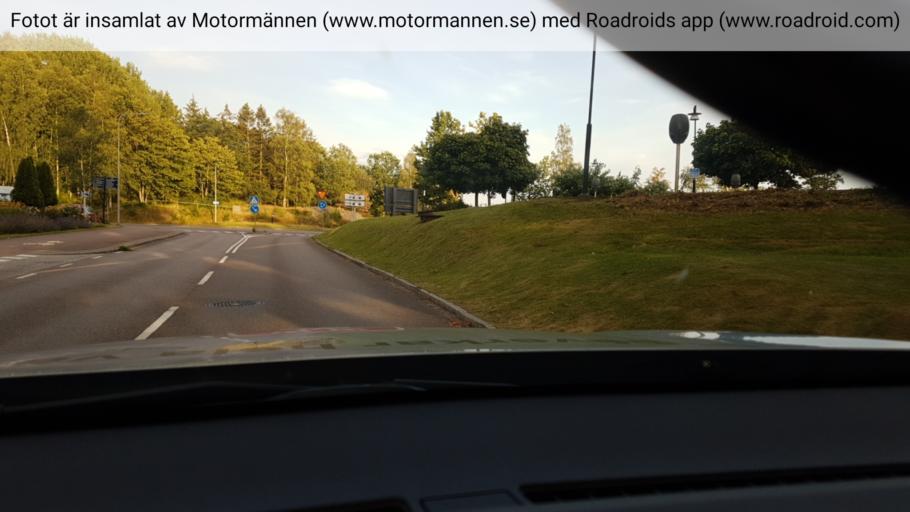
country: SE
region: Vaestra Goetaland
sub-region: Goteborg
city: Majorna
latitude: 57.7148
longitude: 11.9260
